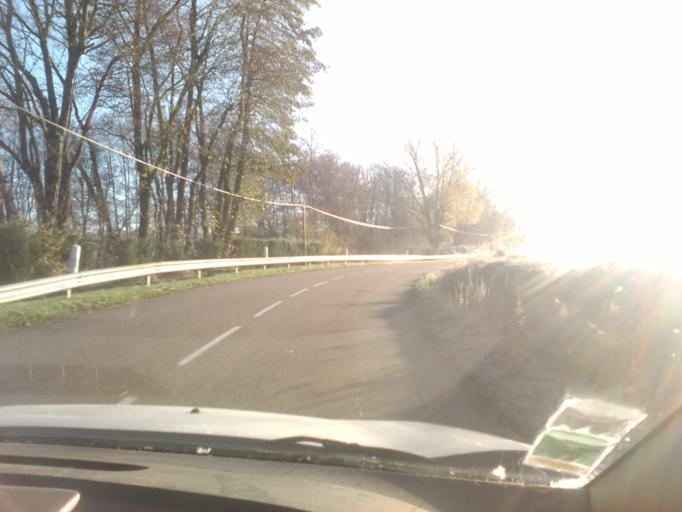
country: FR
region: Lorraine
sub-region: Departement des Vosges
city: Darnieulles
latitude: 48.1581
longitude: 6.2330
